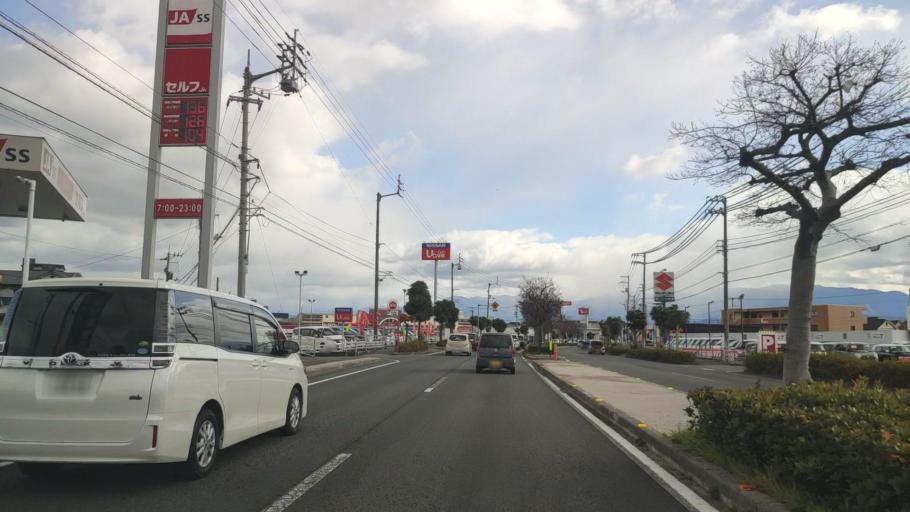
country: JP
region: Ehime
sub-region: Shikoku-chuo Shi
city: Matsuyama
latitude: 33.8192
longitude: 132.7911
